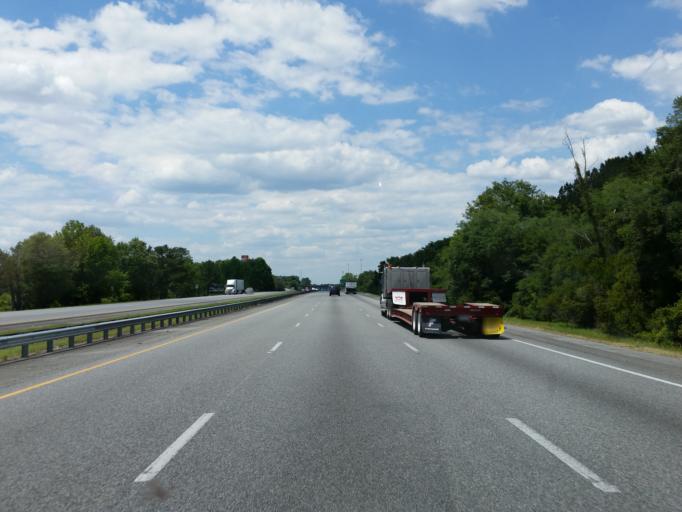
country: US
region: Georgia
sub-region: Echols County
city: Statenville
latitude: 30.6371
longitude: -83.1831
